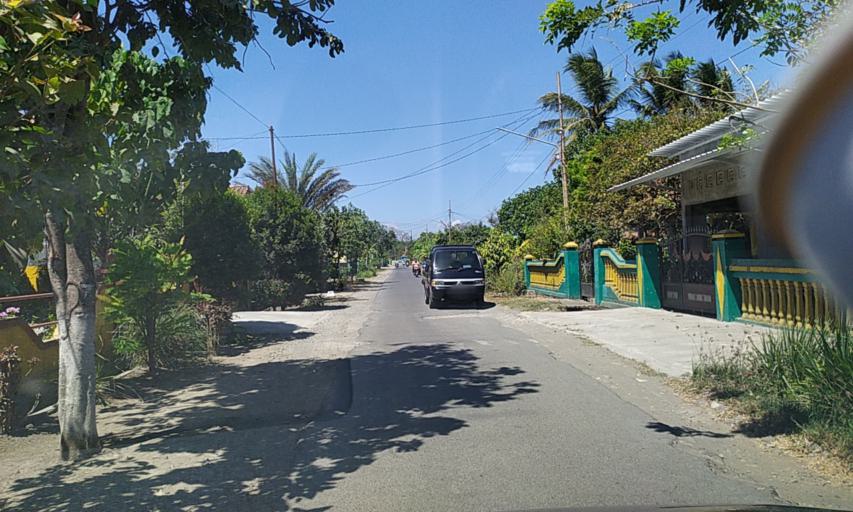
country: ID
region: Central Java
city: Adipala
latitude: -7.6617
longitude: 109.1109
